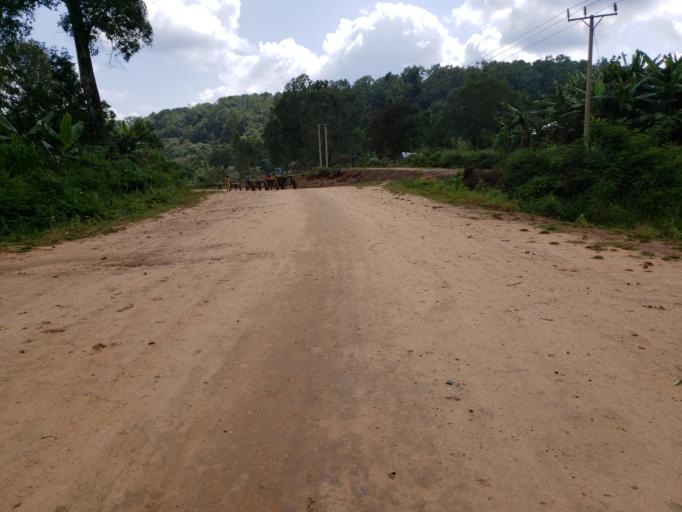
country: ET
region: Oromiya
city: Dodola
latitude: 6.4552
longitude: 39.5693
